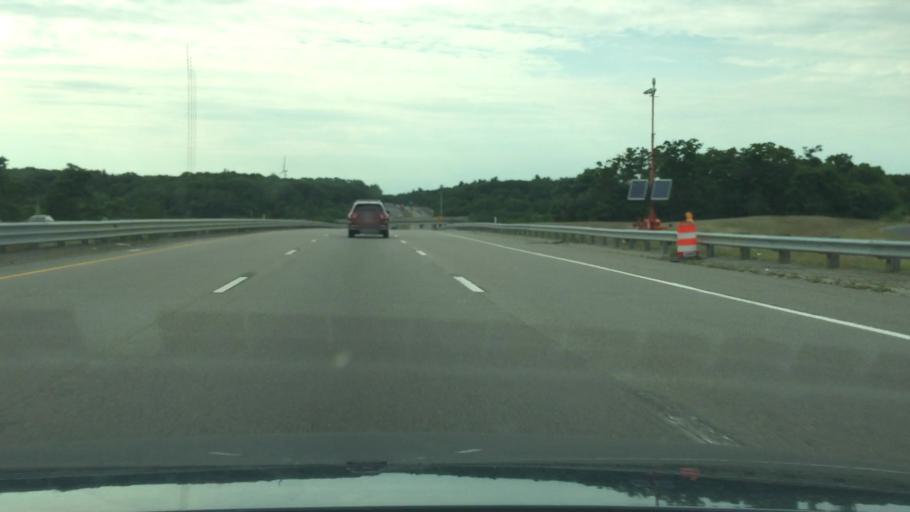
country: US
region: Massachusetts
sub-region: Plymouth County
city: North Plymouth
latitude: 41.9635
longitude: -70.6934
